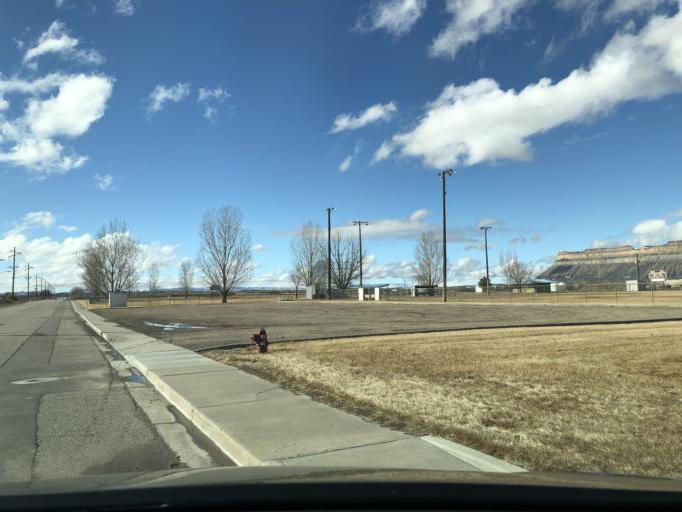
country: US
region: Utah
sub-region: Carbon County
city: East Carbon City
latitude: 39.0007
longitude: -110.1623
